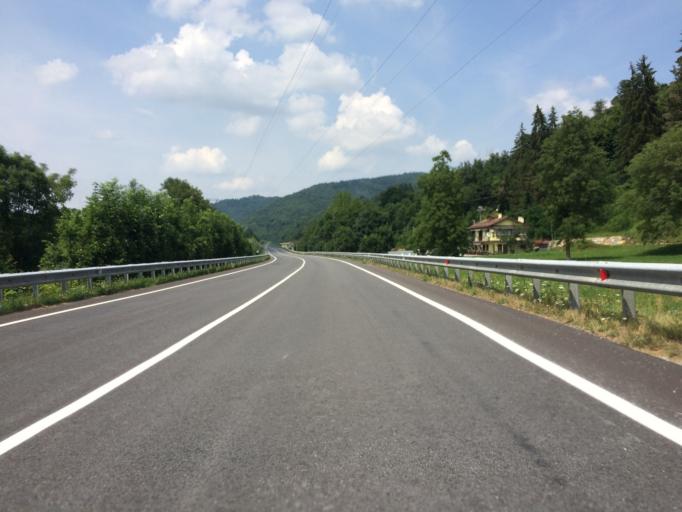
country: IT
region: Piedmont
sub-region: Provincia di Cuneo
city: Robilante
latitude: 44.2875
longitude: 7.5194
